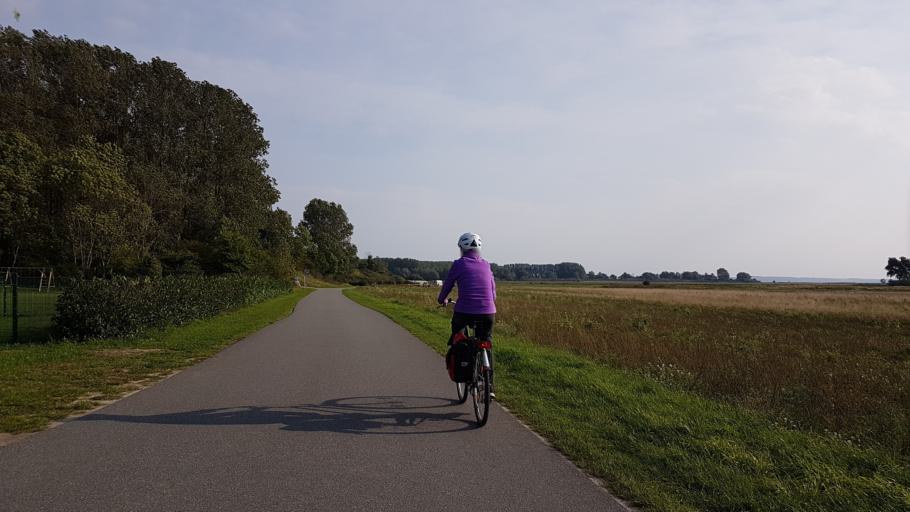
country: DE
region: Mecklenburg-Vorpommern
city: Glowe
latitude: 54.5653
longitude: 13.4757
